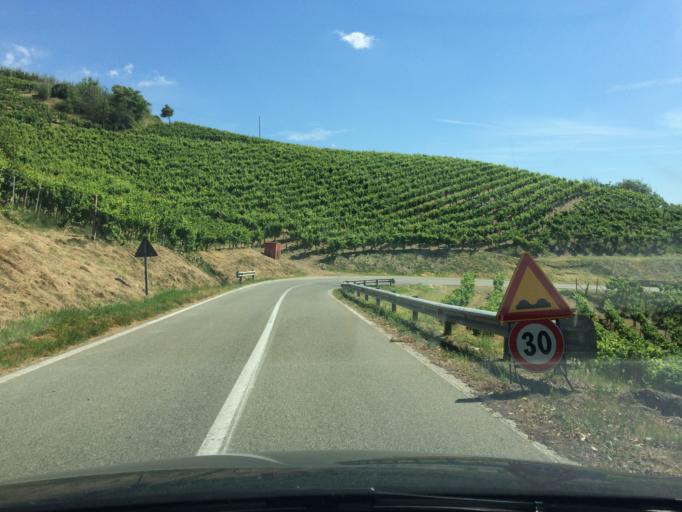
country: IT
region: Piedmont
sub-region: Provincia di Asti
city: Castel Rocchero
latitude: 44.7269
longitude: 8.4279
